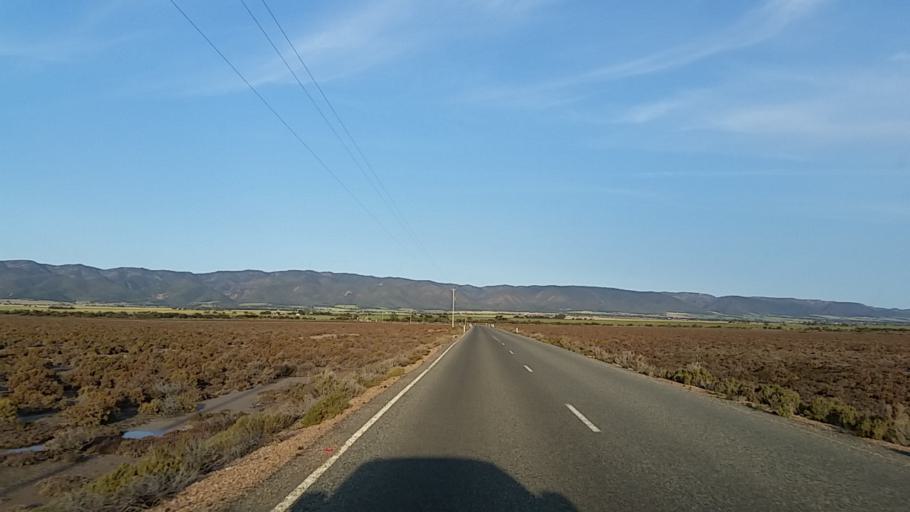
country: AU
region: South Australia
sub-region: Port Pirie City and Dists
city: Port Pirie
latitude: -33.1032
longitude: 138.0450
